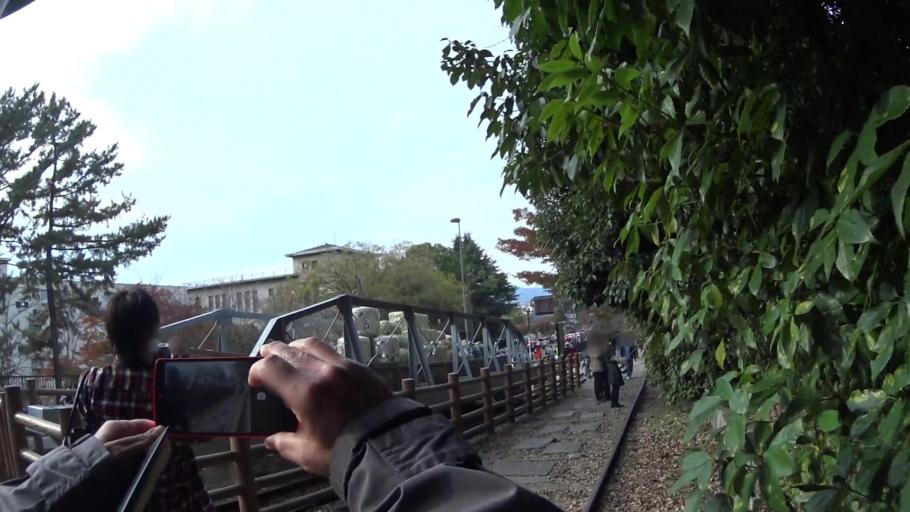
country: JP
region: Kyoto
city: Kyoto
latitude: 35.0099
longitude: 135.7893
